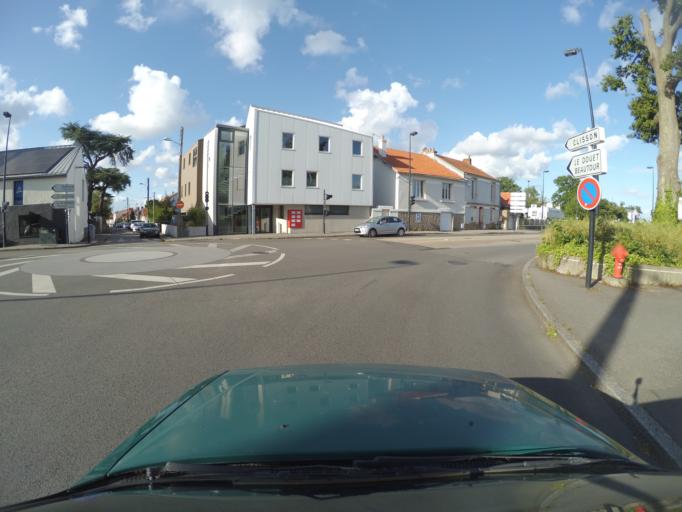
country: FR
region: Pays de la Loire
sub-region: Departement de la Loire-Atlantique
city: Saint-Sebastien-sur-Loire
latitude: 47.1897
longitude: -1.5187
